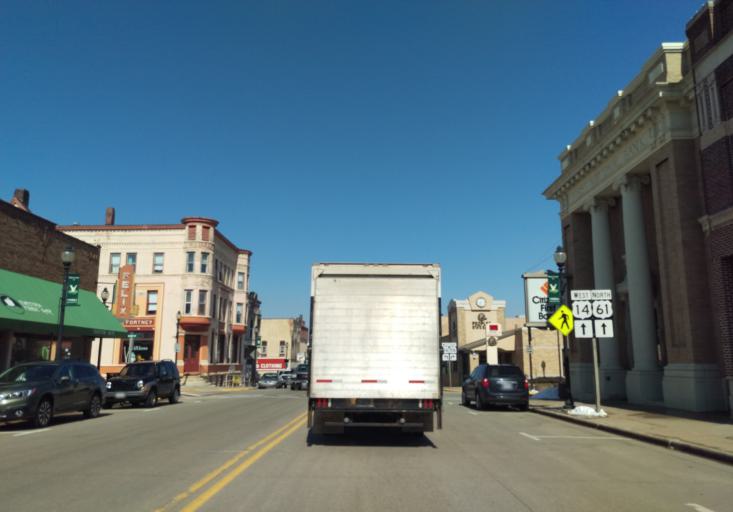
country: US
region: Wisconsin
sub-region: Vernon County
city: Viroqua
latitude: 43.5559
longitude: -90.8893
